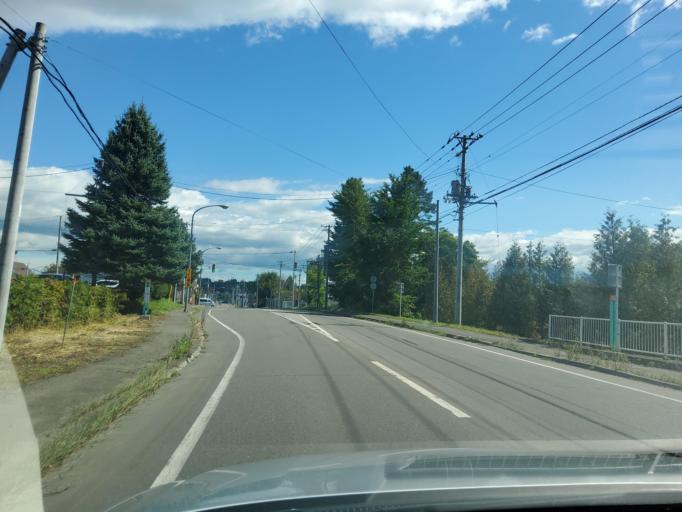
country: JP
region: Hokkaido
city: Obihiro
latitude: 42.9519
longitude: 143.2001
